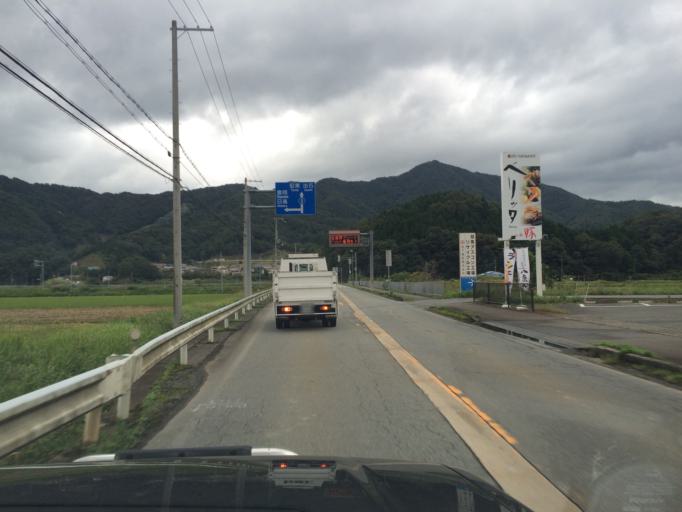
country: JP
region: Hyogo
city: Toyooka
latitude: 35.4328
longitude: 134.7960
